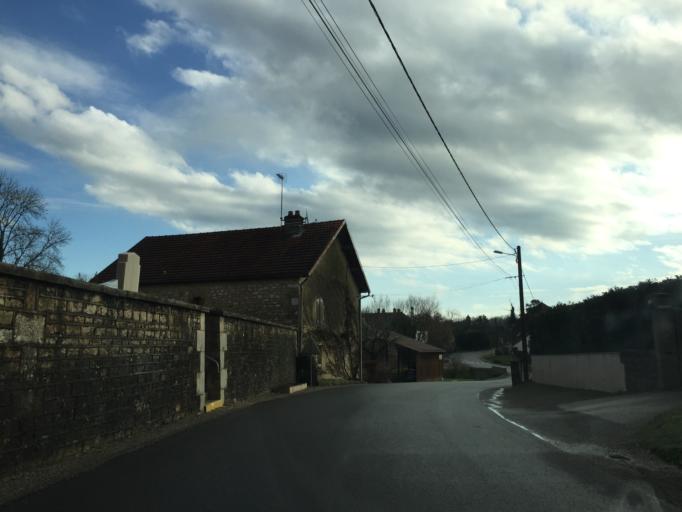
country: FR
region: Franche-Comte
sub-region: Departement du Jura
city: Mont-sous-Vaudrey
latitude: 46.9800
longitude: 5.6220
